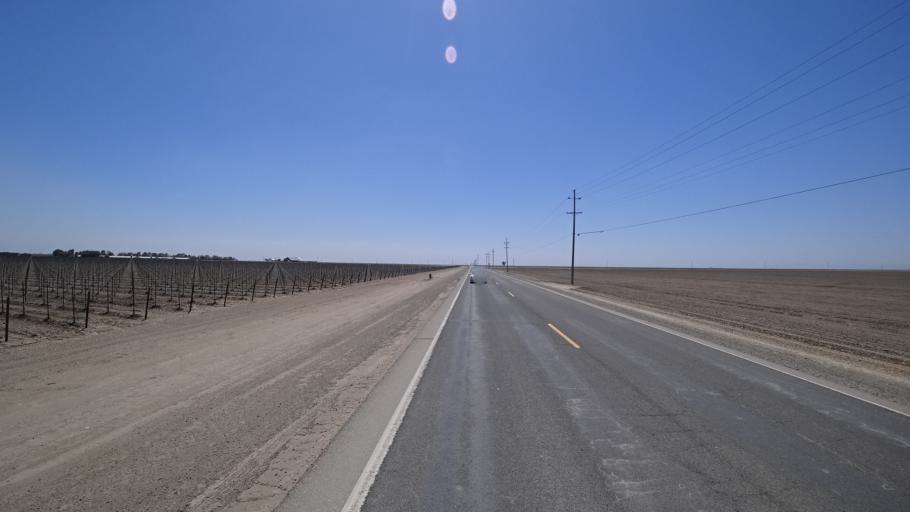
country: US
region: California
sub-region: Kings County
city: Corcoran
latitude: 36.1202
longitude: -119.6444
